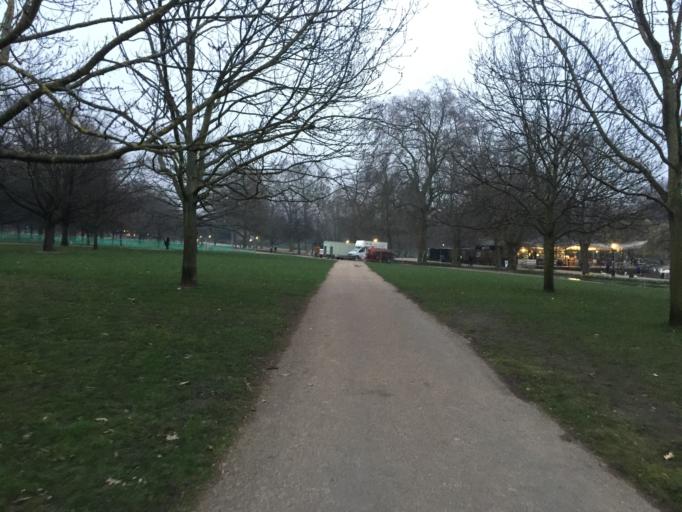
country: GB
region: England
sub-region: Greater London
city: Chelsea
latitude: 51.5060
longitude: -0.1606
